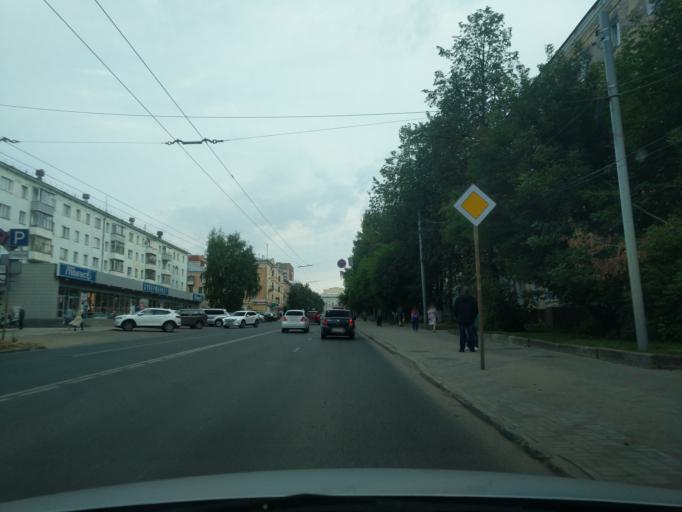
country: RU
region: Kirov
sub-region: Kirovo-Chepetskiy Rayon
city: Kirov
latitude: 58.6101
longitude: 49.6674
